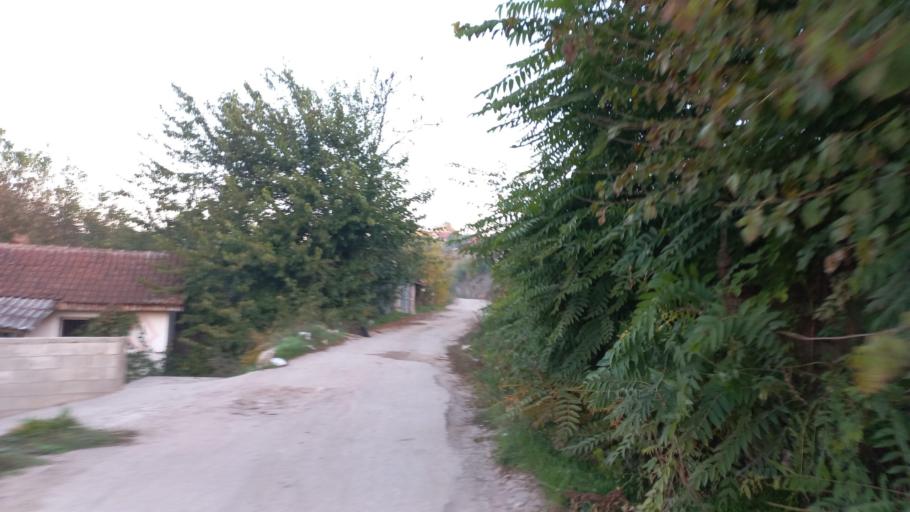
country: MK
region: Kumanovo
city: Kumanovo
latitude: 42.1379
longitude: 21.7284
